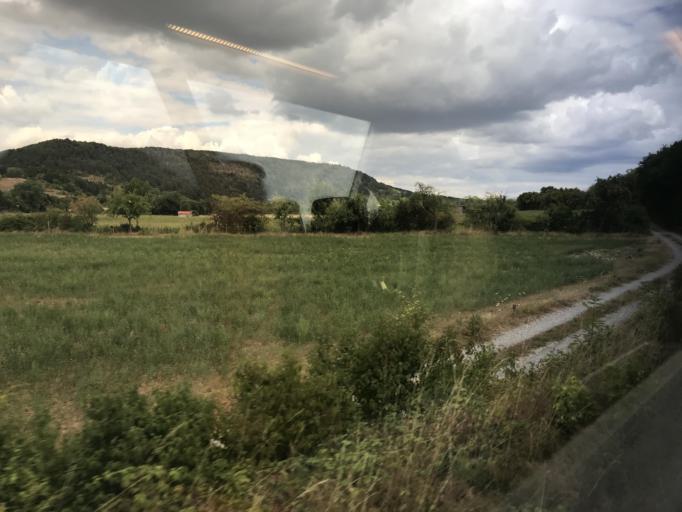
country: DE
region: Bavaria
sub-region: Regierungsbezirk Unterfranken
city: Elfershausen
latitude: 50.1315
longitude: 9.9512
